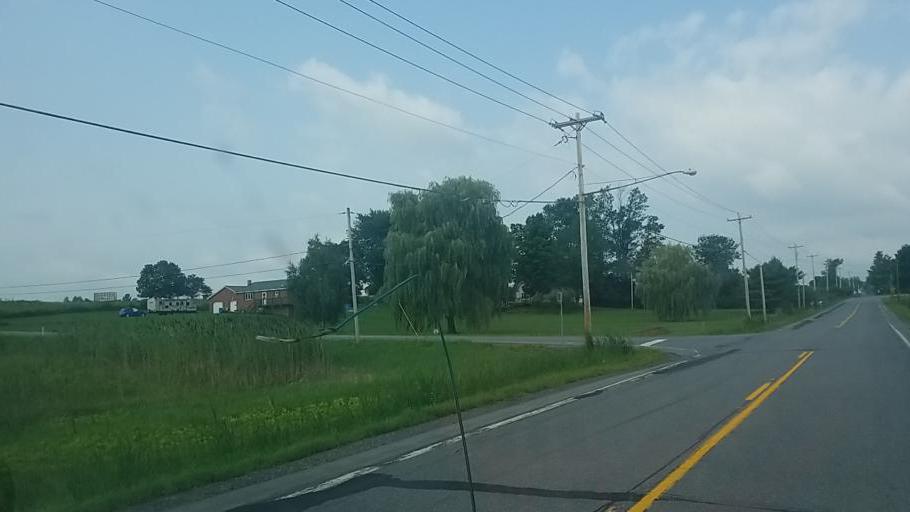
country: US
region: New York
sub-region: Fulton County
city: Johnstown
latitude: 43.0194
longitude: -74.4016
